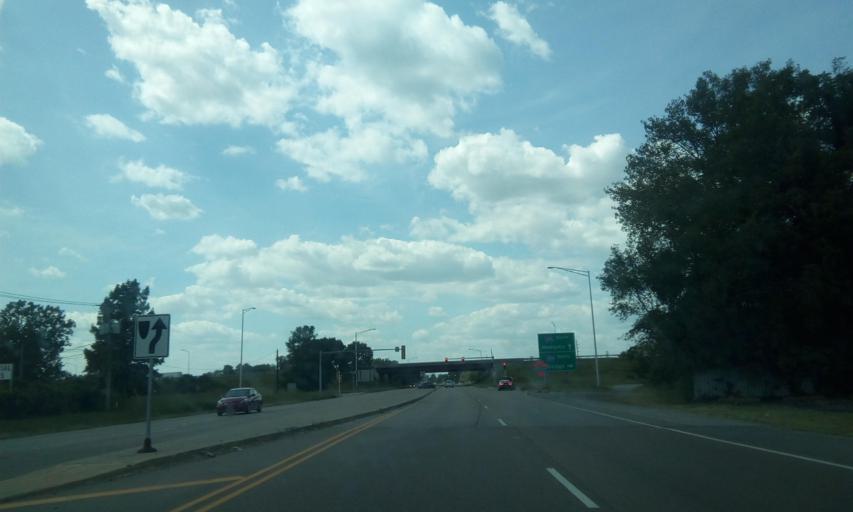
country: US
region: Illinois
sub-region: Saint Clair County
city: Caseyville
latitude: 38.6599
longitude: -90.0282
